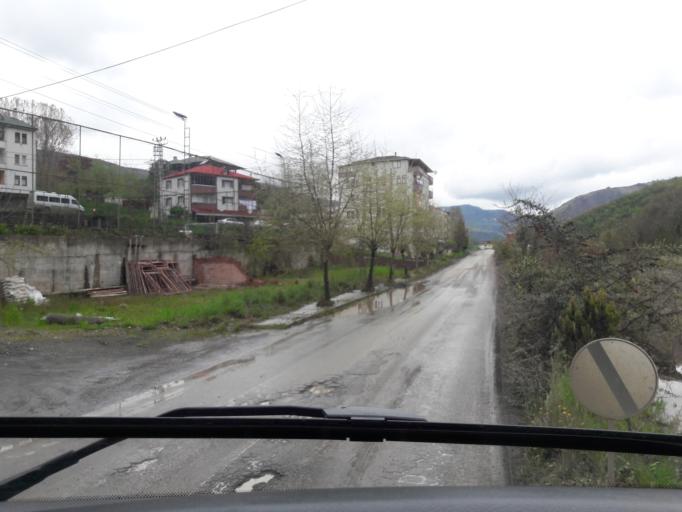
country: TR
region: Trabzon
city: Duzkoy
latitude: 40.9269
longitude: 39.4934
